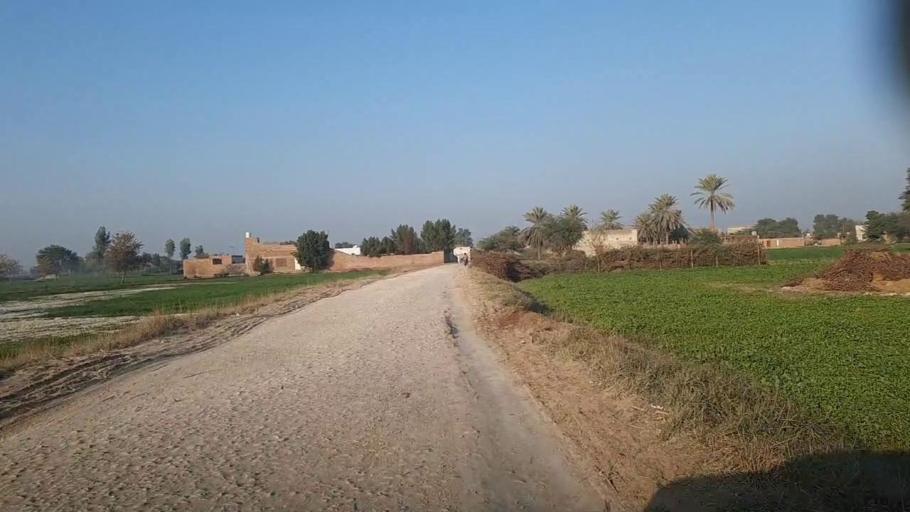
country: PK
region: Sindh
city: Khairpur
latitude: 28.0743
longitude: 69.7449
